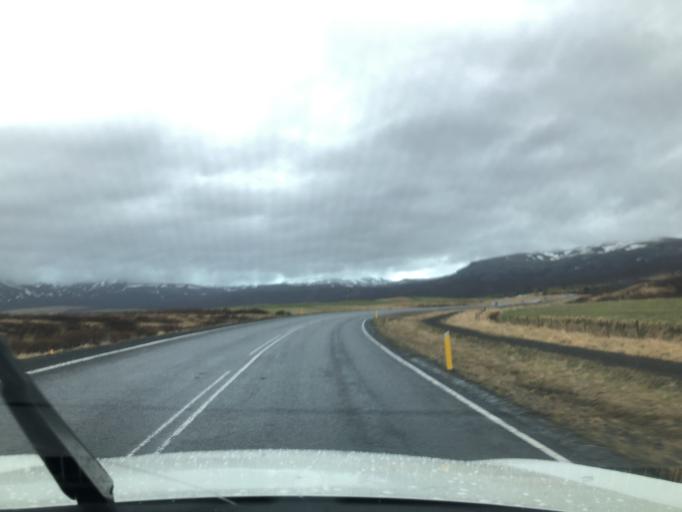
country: IS
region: South
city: Selfoss
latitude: 64.2254
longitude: -20.6315
